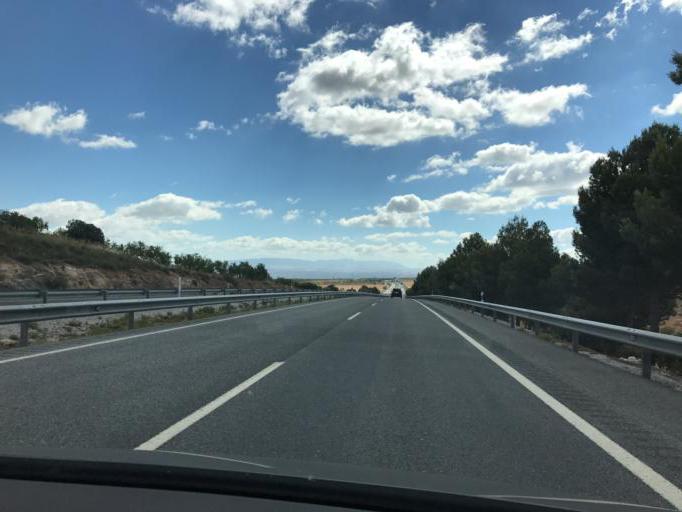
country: ES
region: Andalusia
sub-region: Provincia de Granada
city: Zujar
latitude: 37.4907
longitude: -2.8399
